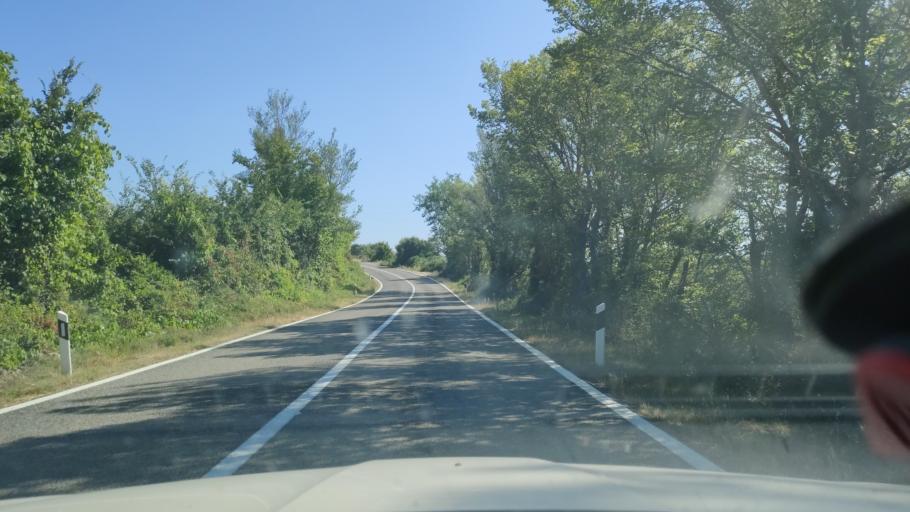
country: HR
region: Sibensko-Kniniska
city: Kistanje
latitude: 43.9580
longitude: 15.8625
